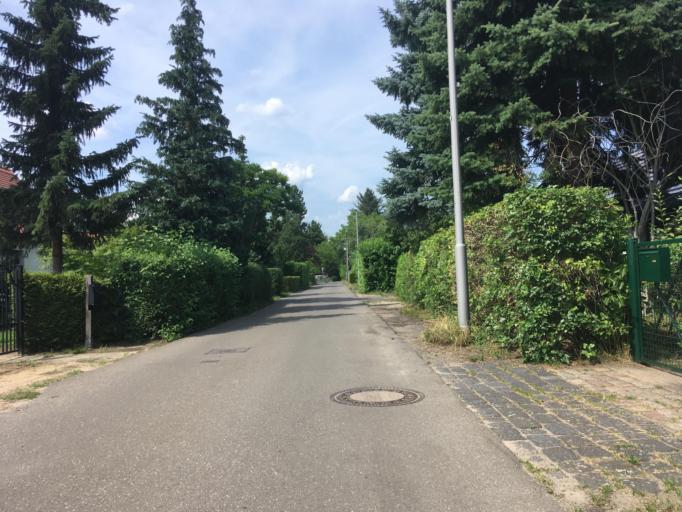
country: DE
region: Berlin
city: Berlin Koepenick
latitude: 52.4351
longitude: 13.5846
